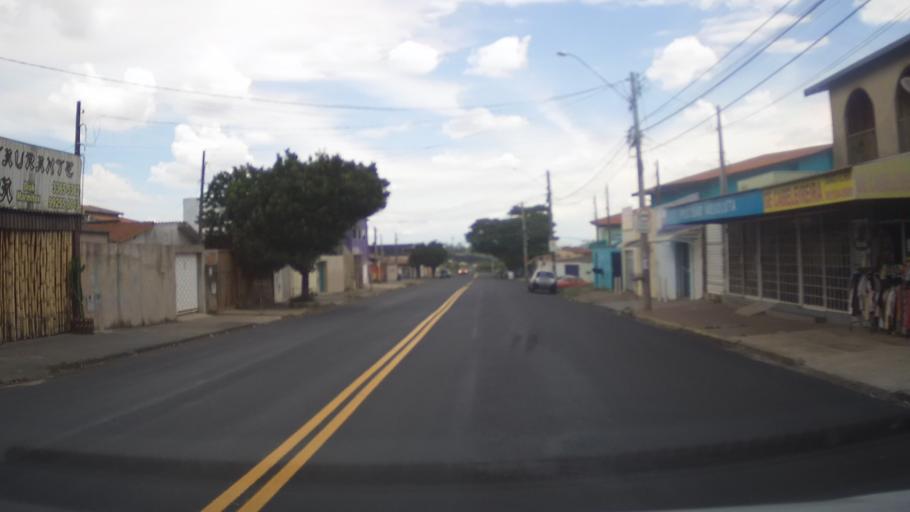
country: BR
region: Sao Paulo
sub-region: Campinas
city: Campinas
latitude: -22.9223
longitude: -47.0172
